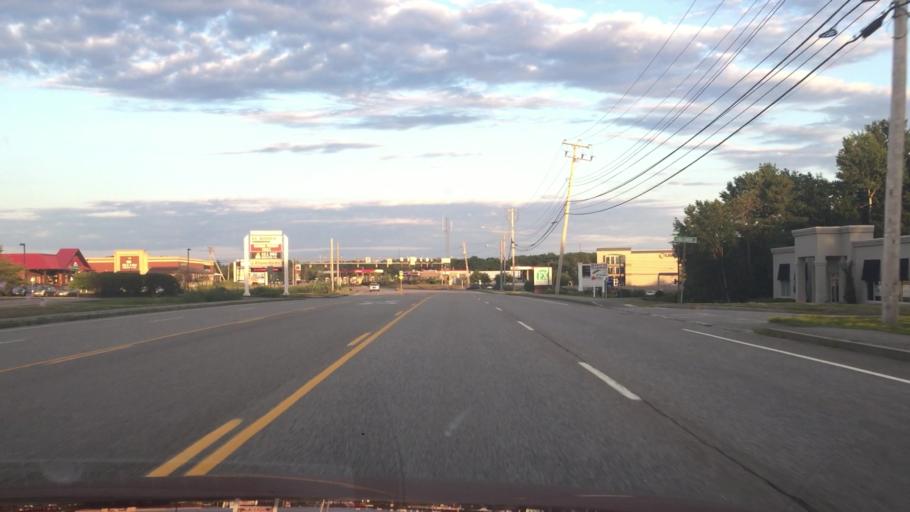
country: US
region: Maine
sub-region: Cumberland County
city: South Portland Gardens
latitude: 43.6362
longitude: -70.3215
